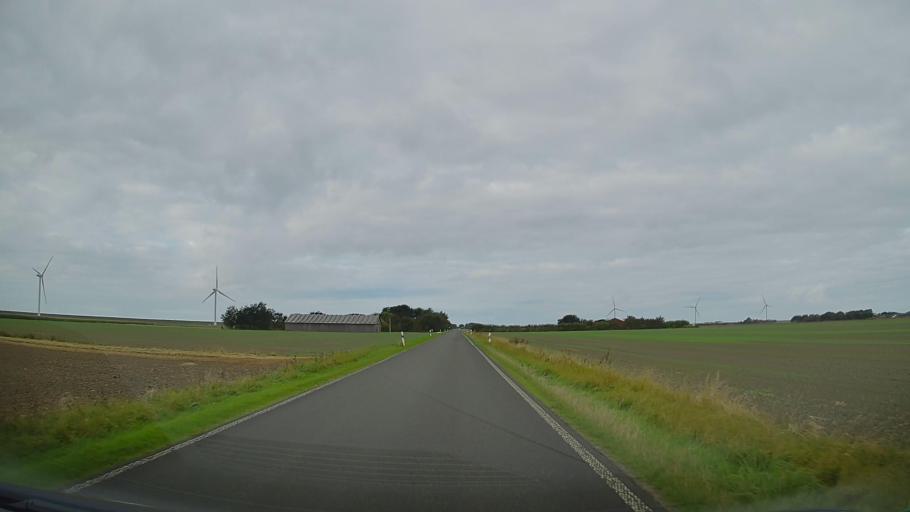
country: DE
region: Schleswig-Holstein
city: Friedrich-Wilhelm-Lubke-Koog
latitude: 54.8375
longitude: 8.6363
